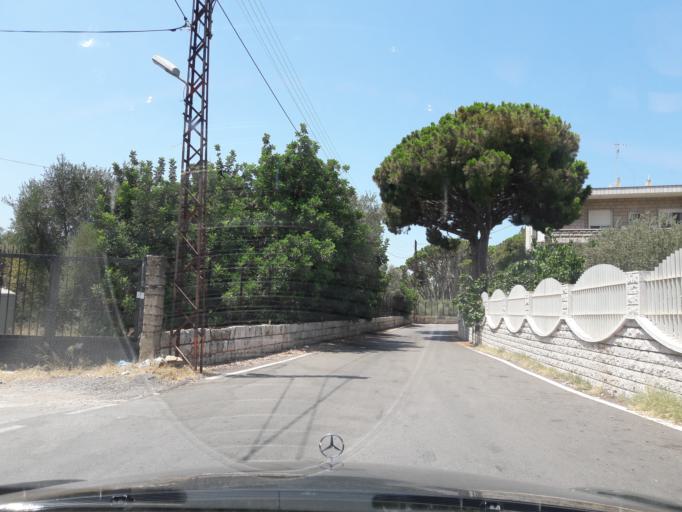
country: LB
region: Mont-Liban
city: Djounie
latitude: 33.9343
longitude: 35.6206
